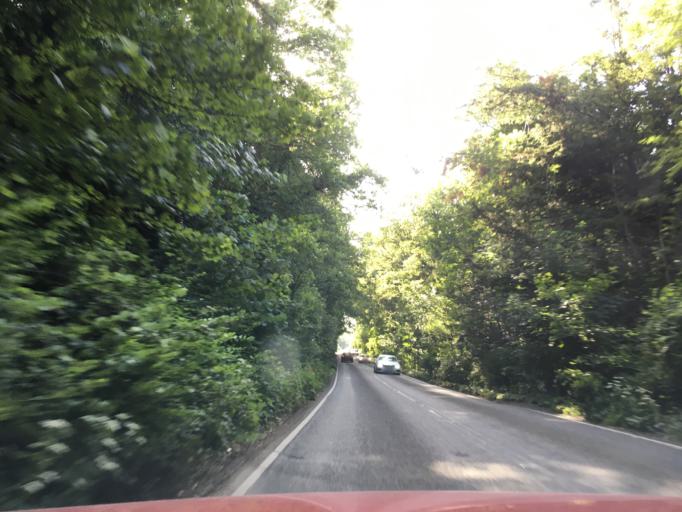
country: GB
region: England
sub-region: Oxfordshire
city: Somerton
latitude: 51.9199
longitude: -1.3077
